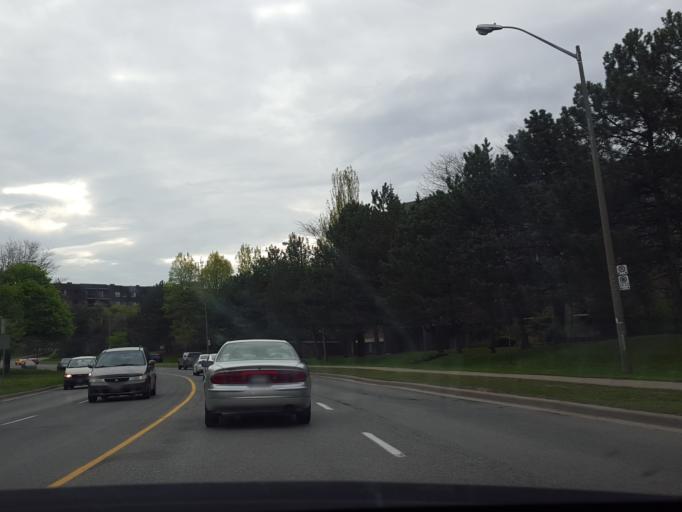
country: CA
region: Ontario
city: Willowdale
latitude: 43.7931
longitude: -79.3361
